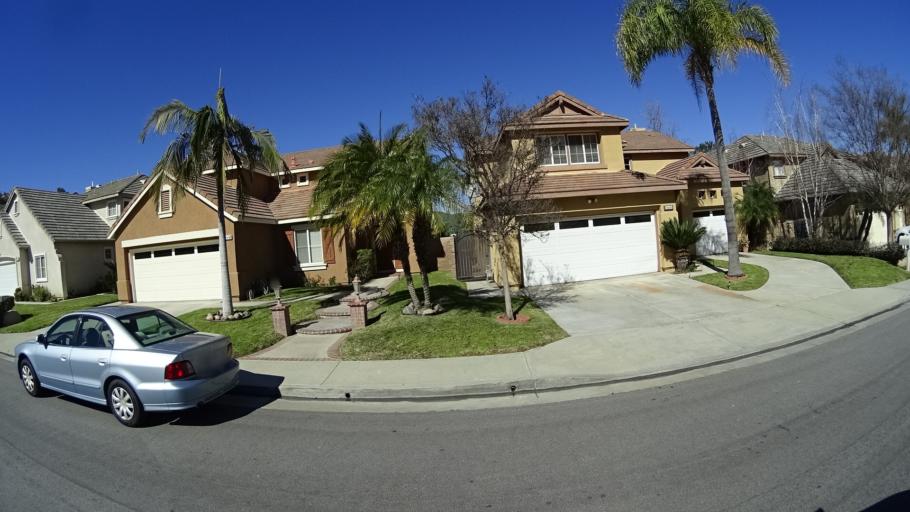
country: US
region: California
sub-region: Orange County
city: Yorba Linda
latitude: 33.8620
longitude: -117.7232
